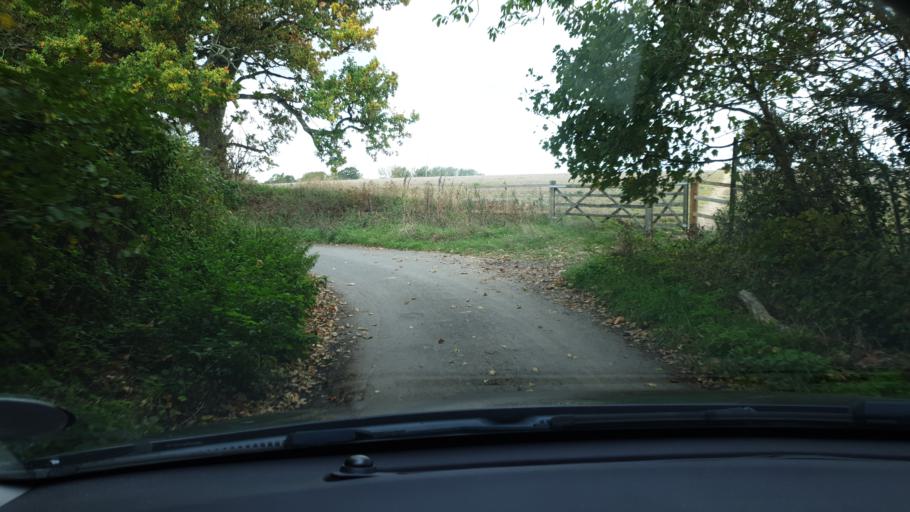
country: GB
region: England
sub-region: Essex
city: Mistley
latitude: 51.9335
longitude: 1.1114
